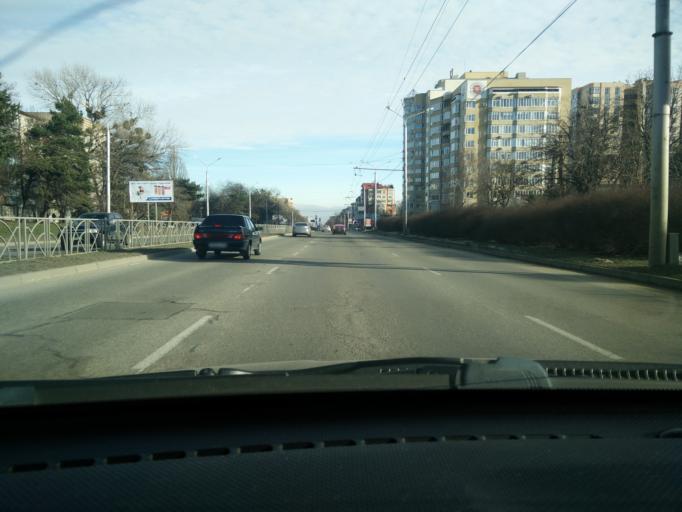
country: RU
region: Stavropol'skiy
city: Stavropol'
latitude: 45.0335
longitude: 41.9556
